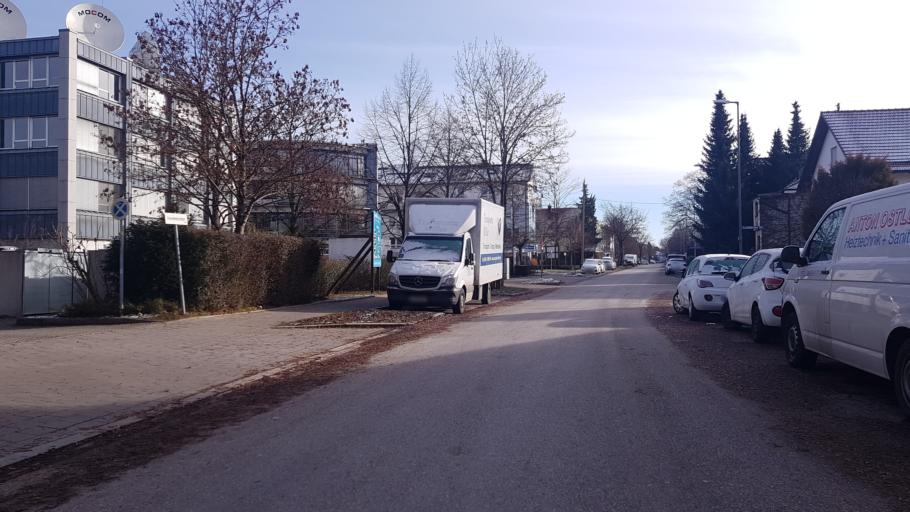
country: DE
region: Bavaria
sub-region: Upper Bavaria
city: Bogenhausen
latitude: 48.1347
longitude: 11.6570
